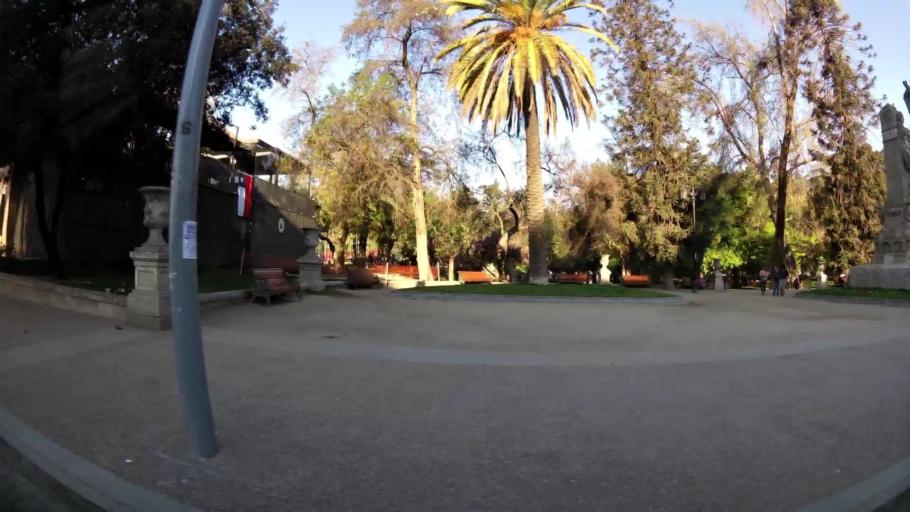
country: CL
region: Santiago Metropolitan
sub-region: Provincia de Santiago
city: Santiago
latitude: -33.4352
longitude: -70.6428
